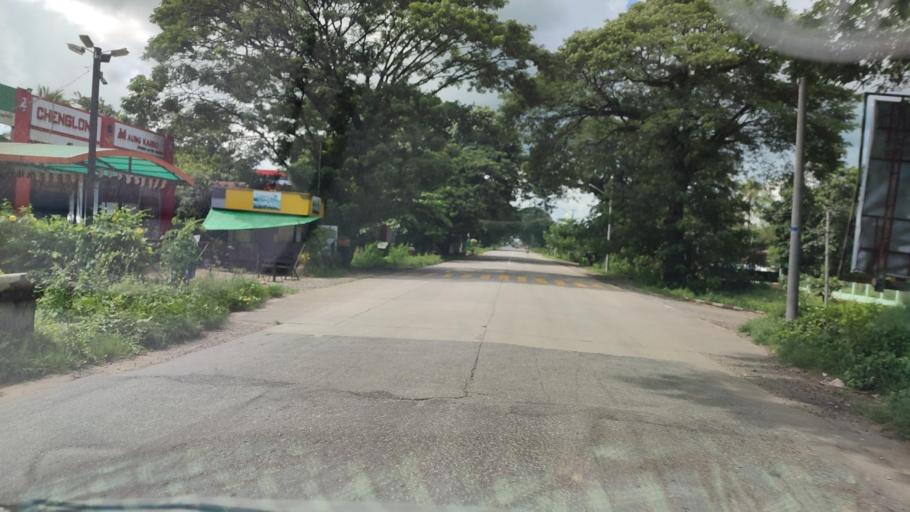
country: MM
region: Bago
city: Nyaunglebin
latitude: 17.9606
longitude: 96.7130
